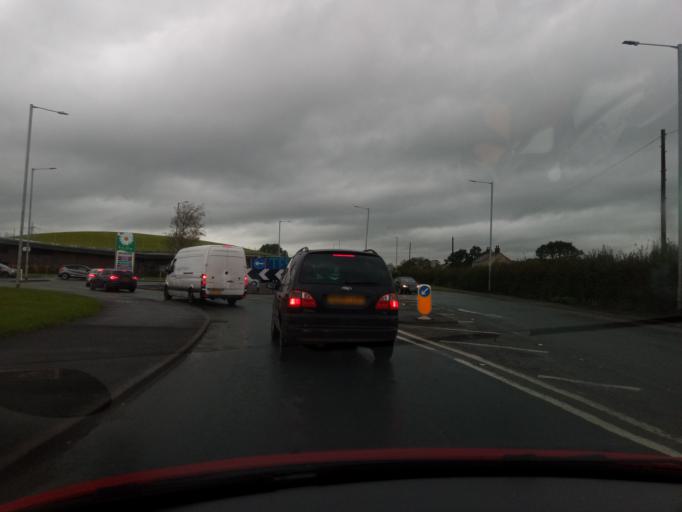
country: GB
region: England
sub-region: Lancashire
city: Catterall
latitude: 53.8614
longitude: -2.7444
